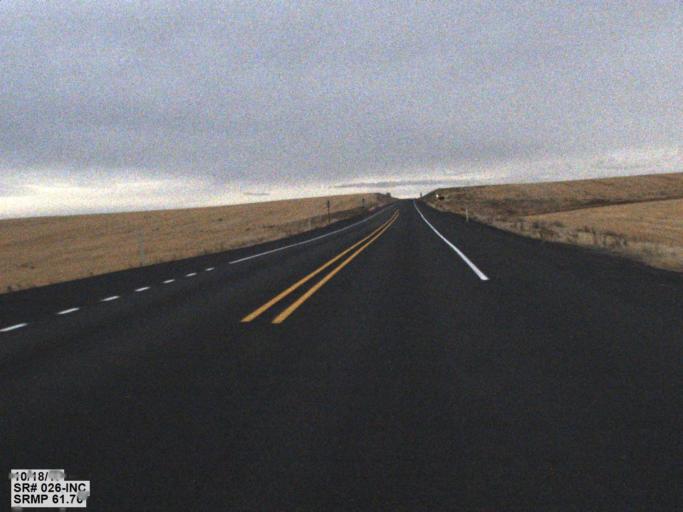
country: US
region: Washington
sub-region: Franklin County
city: Connell
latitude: 46.7938
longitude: -118.7353
